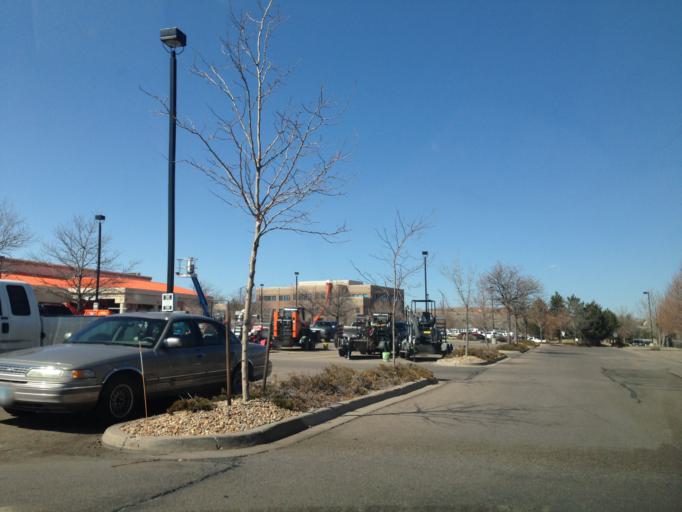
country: US
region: Colorado
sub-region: Boulder County
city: Superior
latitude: 39.9609
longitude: -105.1685
